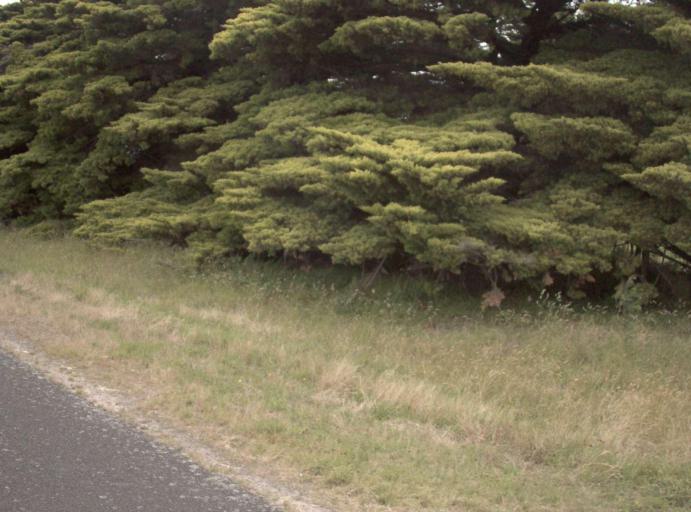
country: AU
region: Victoria
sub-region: Wellington
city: Sale
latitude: -38.5890
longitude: 146.8887
